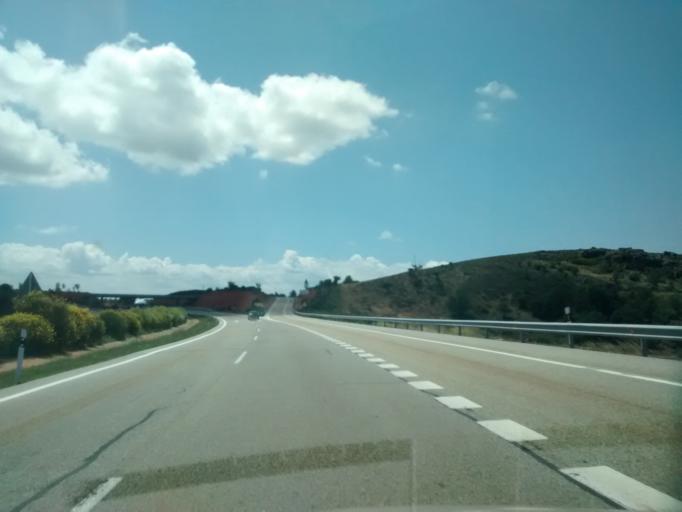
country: ES
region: Castille and Leon
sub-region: Provincia de Leon
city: Brazuelo
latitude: 42.4950
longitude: -6.1278
